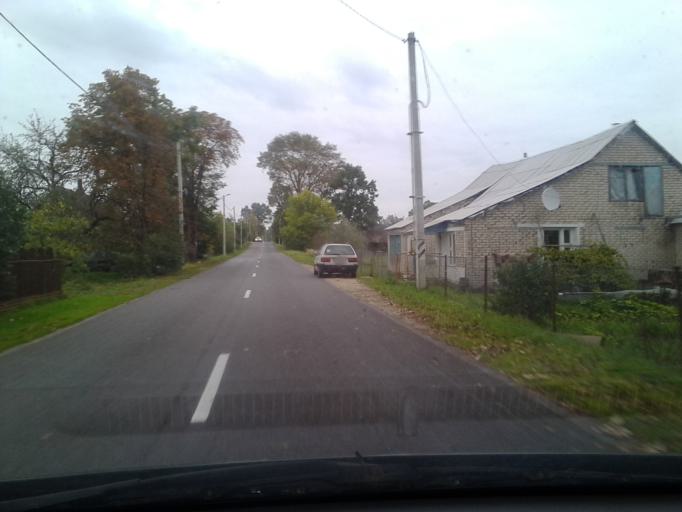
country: BY
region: Vitebsk
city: Pastavy
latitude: 55.1412
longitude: 26.9534
